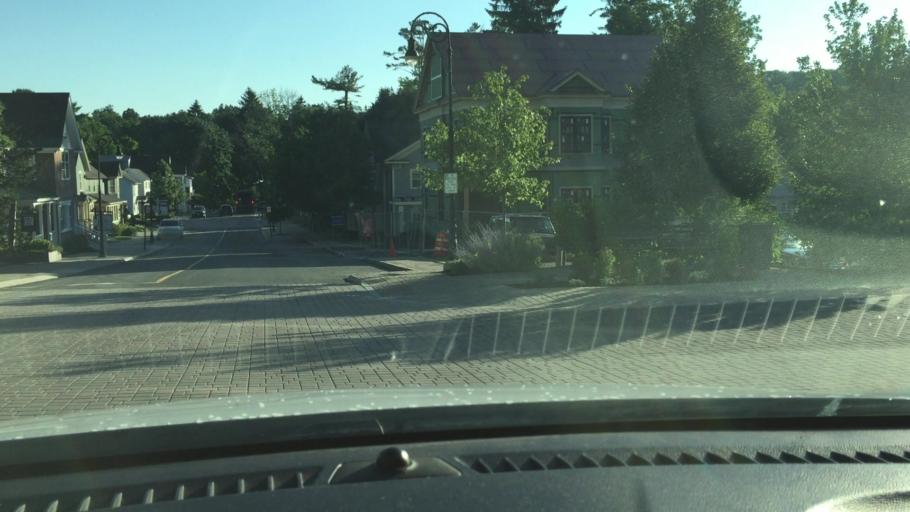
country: US
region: Massachusetts
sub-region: Berkshire County
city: Lenox
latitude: 42.3576
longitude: -73.2829
